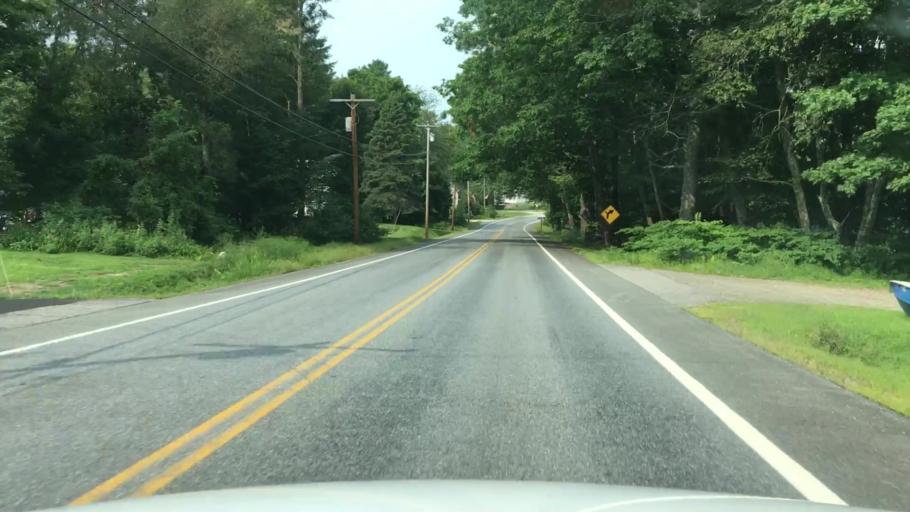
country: US
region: Maine
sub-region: Kennebec County
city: Wayne
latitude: 44.3482
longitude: -70.0630
